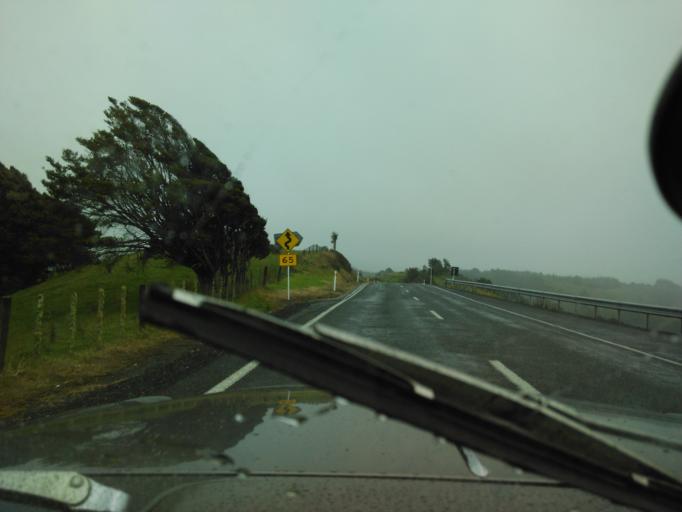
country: NZ
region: Auckland
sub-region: Auckland
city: Wellsford
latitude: -36.3518
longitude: 174.4716
